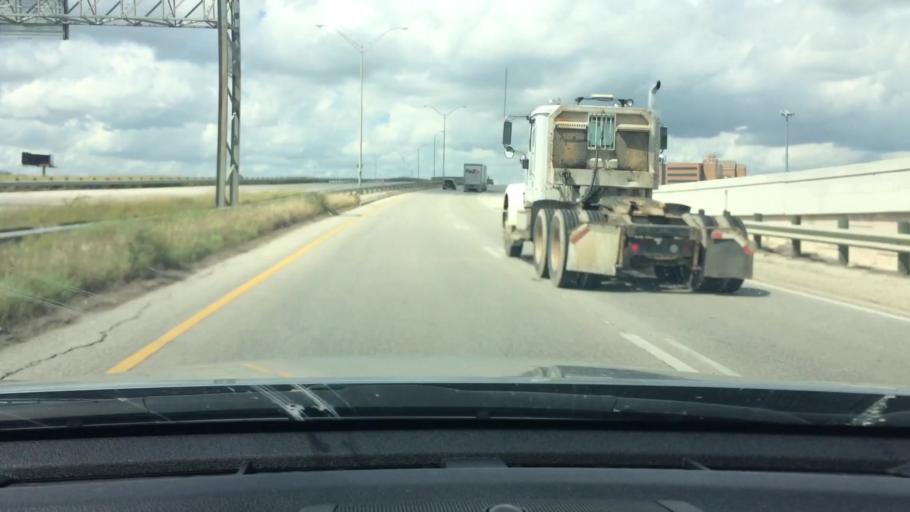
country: US
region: Texas
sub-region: Bexar County
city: Kirby
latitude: 29.4534
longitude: -98.4097
